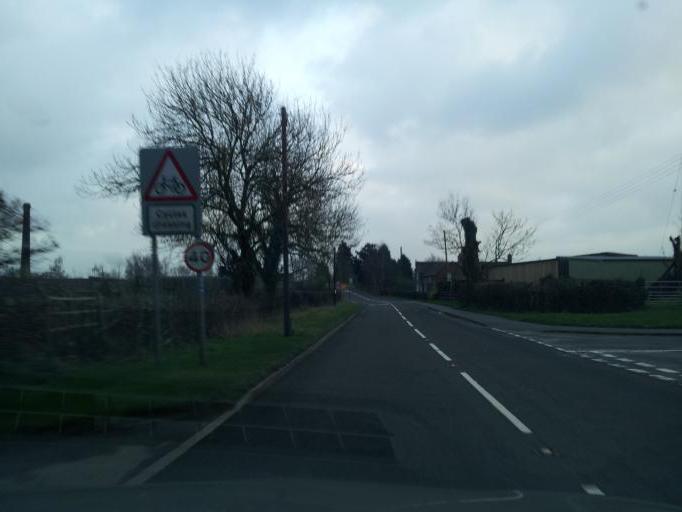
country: GB
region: England
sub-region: Derbyshire
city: Etwall
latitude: 52.8653
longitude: -1.6162
